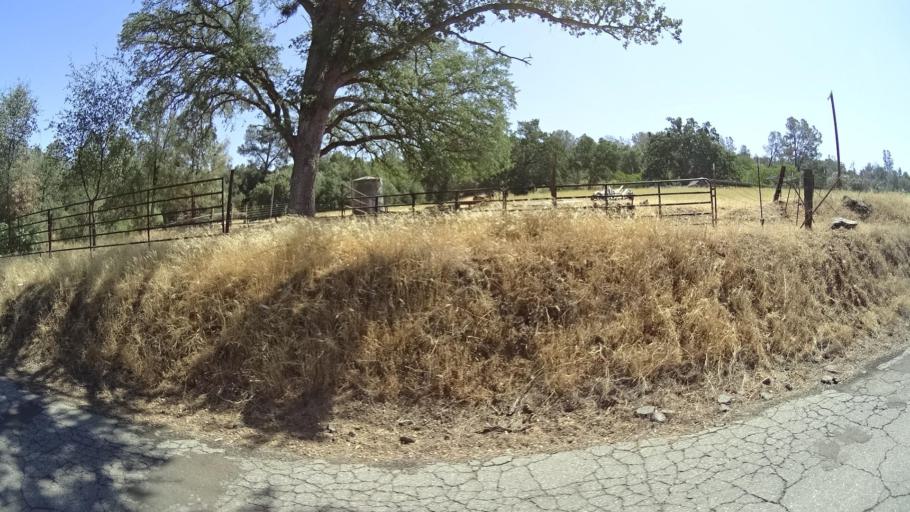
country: US
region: California
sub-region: Mariposa County
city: Mariposa
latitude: 37.4149
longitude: -119.9648
